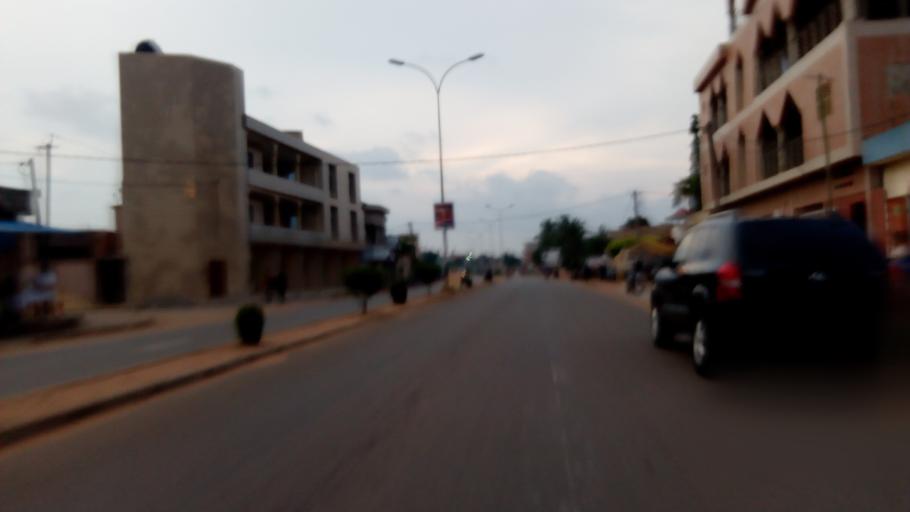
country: TG
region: Maritime
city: Lome
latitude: 6.2156
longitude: 1.2023
